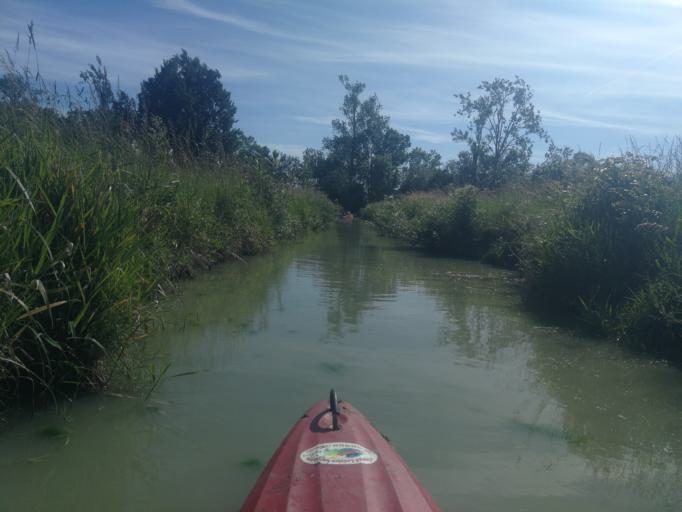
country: FR
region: Poitou-Charentes
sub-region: Departement de la Charente-Maritime
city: Marans
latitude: 46.3642
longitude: -0.9601
